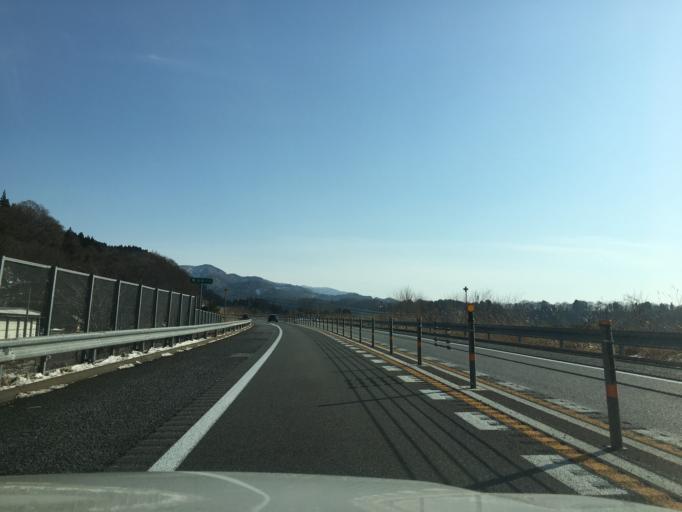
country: JP
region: Yamagata
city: Tsuruoka
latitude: 38.6128
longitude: 139.8417
